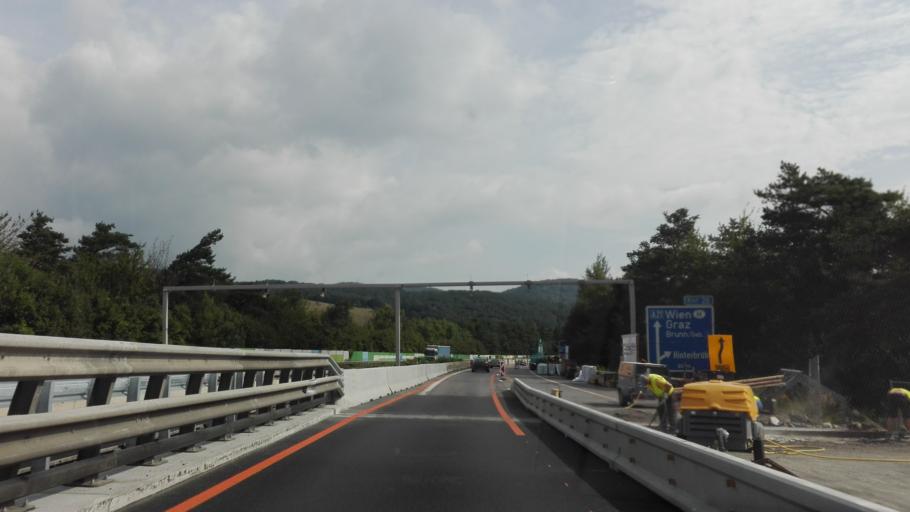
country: AT
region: Lower Austria
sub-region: Politischer Bezirk Modling
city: Gaaden
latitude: 48.0698
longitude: 16.1698
